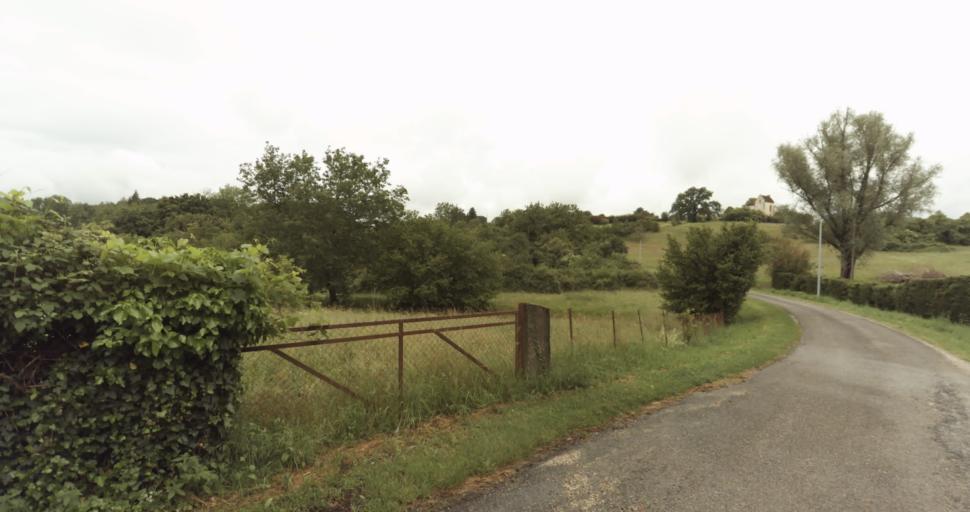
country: FR
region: Aquitaine
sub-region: Departement de la Dordogne
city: Beaumont-du-Perigord
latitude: 44.6825
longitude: 0.8911
